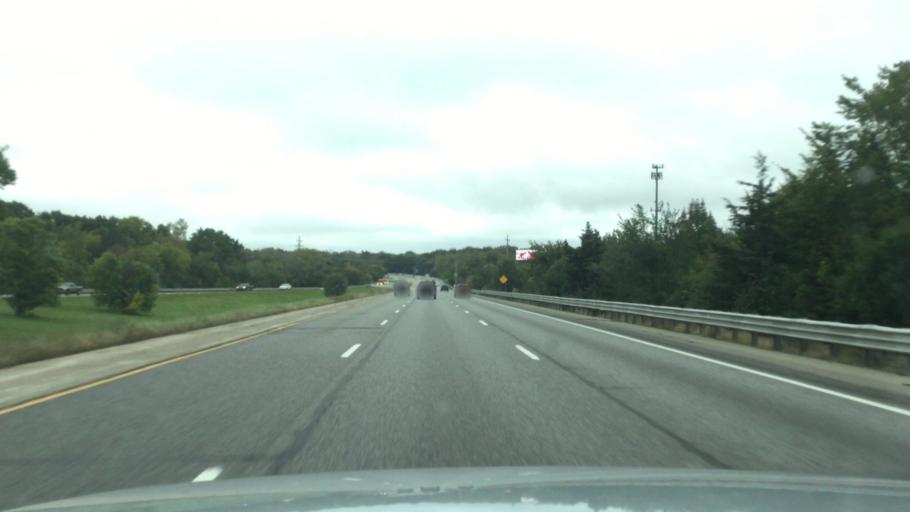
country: US
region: Michigan
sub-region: Genesee County
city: Flint
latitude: 43.0353
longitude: -83.7542
